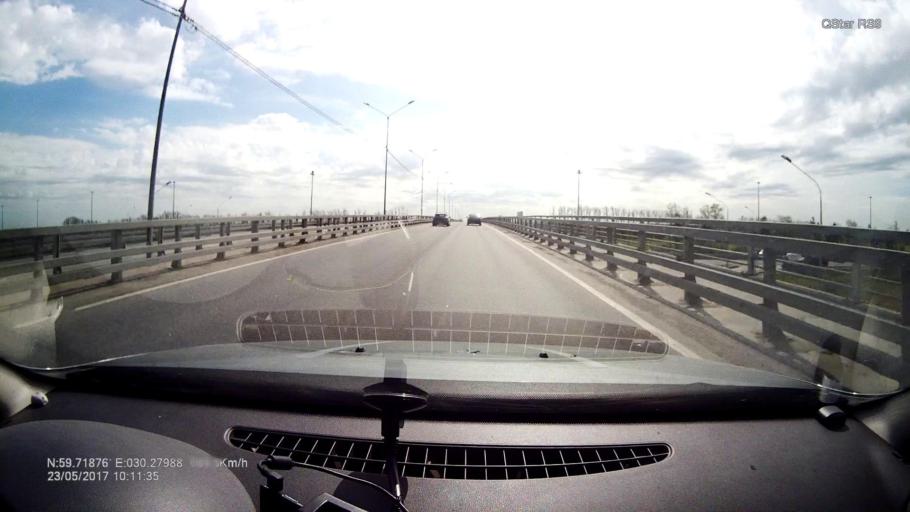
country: RU
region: St.-Petersburg
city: Aleksandrovskaya
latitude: 59.7190
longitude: 30.2797
